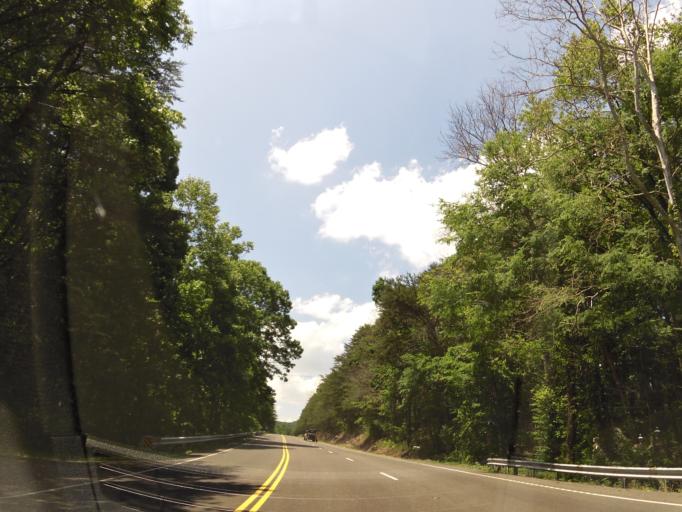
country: US
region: Tennessee
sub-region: Rhea County
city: Dayton
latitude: 35.5144
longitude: -85.0377
